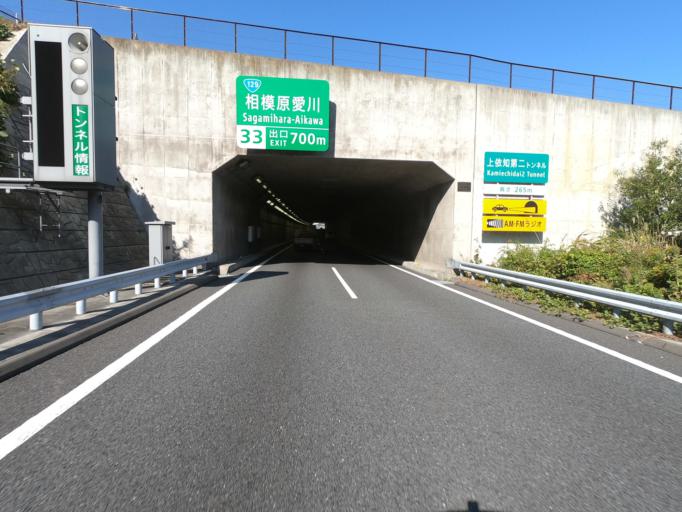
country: JP
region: Kanagawa
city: Zama
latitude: 35.5157
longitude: 139.3598
